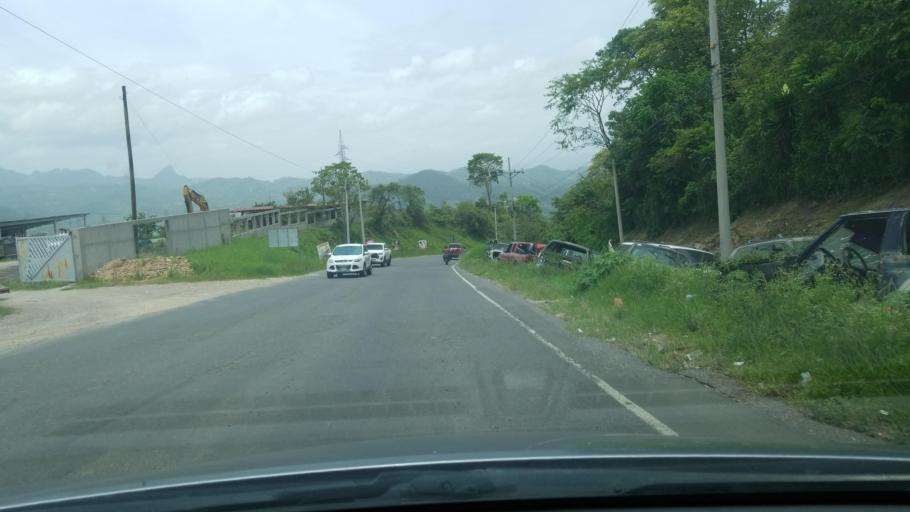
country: HN
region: Copan
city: Santa Rosa de Copan
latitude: 14.7462
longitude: -88.7757
